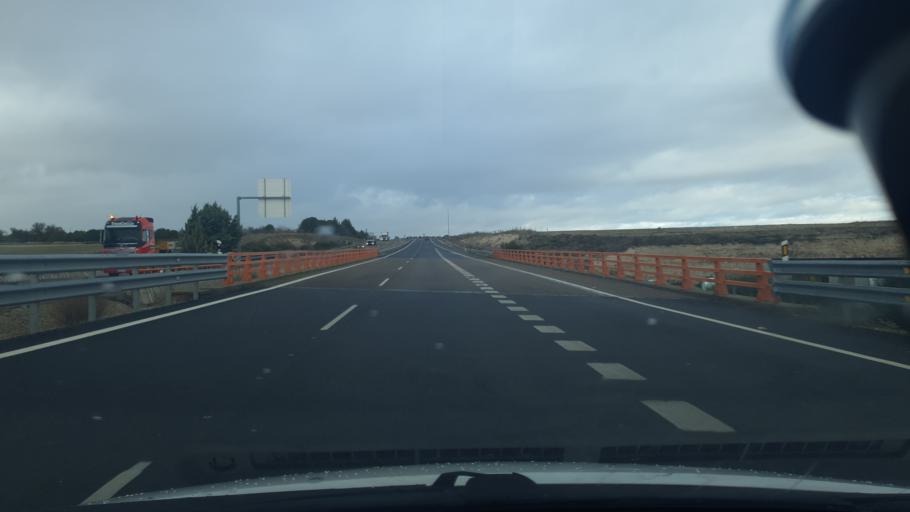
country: ES
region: Castille and Leon
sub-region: Provincia de Segovia
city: Cuellar
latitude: 41.4073
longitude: -4.2969
